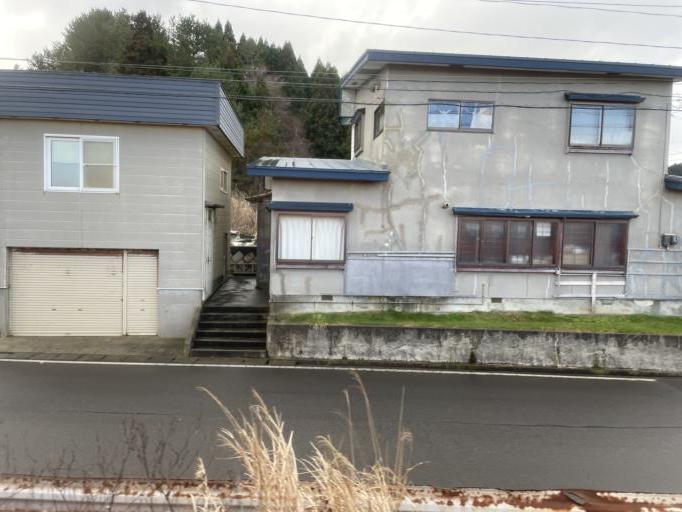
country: JP
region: Aomori
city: Aomori Shi
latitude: 41.0353
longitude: 140.6454
